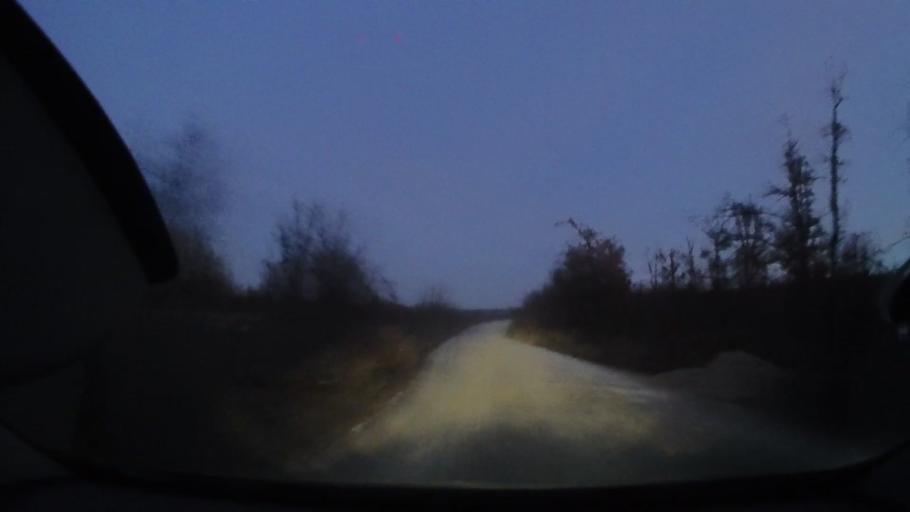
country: RO
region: Bihor
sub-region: Comuna Varciorog
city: Varciorog
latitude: 46.9926
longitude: 22.3146
